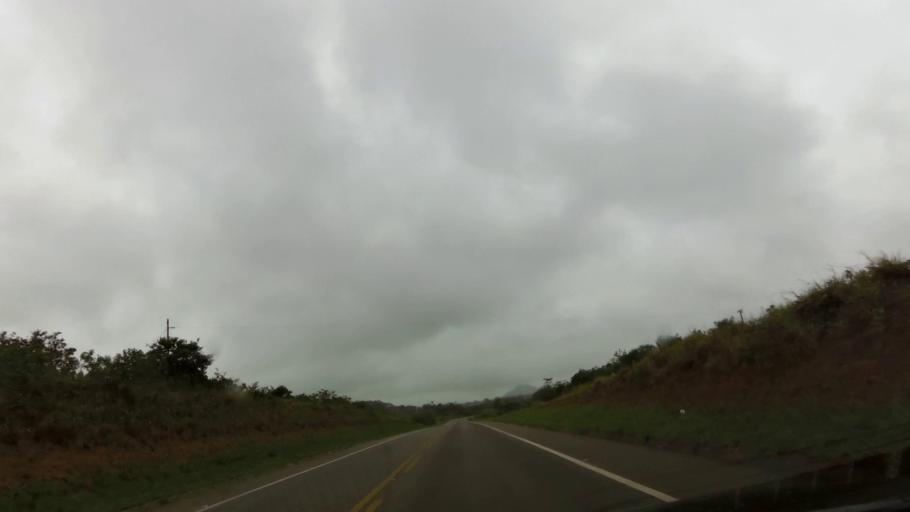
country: BR
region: Espirito Santo
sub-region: Guarapari
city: Guarapari
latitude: -20.7139
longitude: -40.5763
